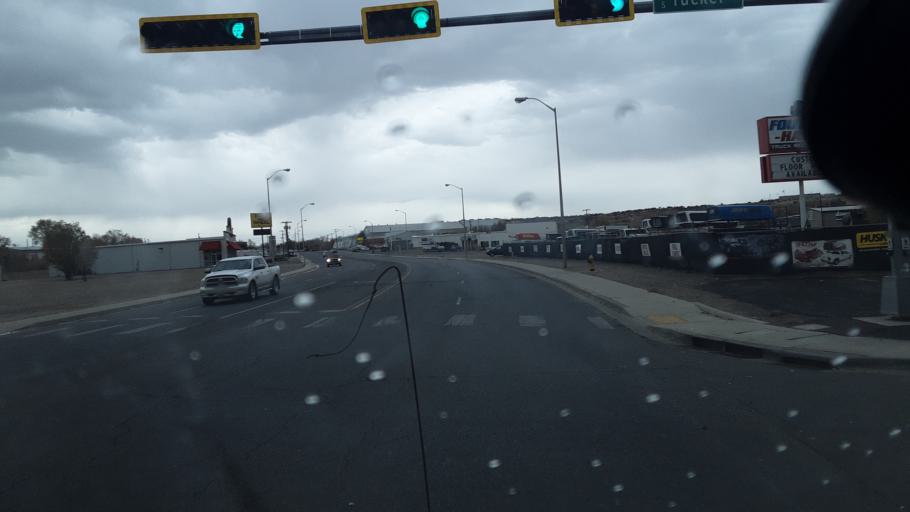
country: US
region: New Mexico
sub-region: San Juan County
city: Farmington
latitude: 36.7372
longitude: -108.1775
